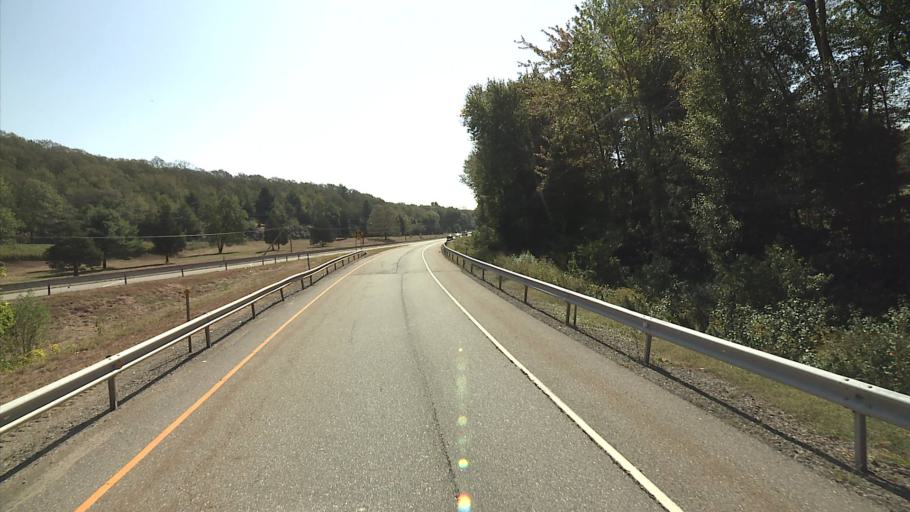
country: US
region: Connecticut
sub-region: New London County
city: Uncasville
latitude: 41.4179
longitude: -72.1107
